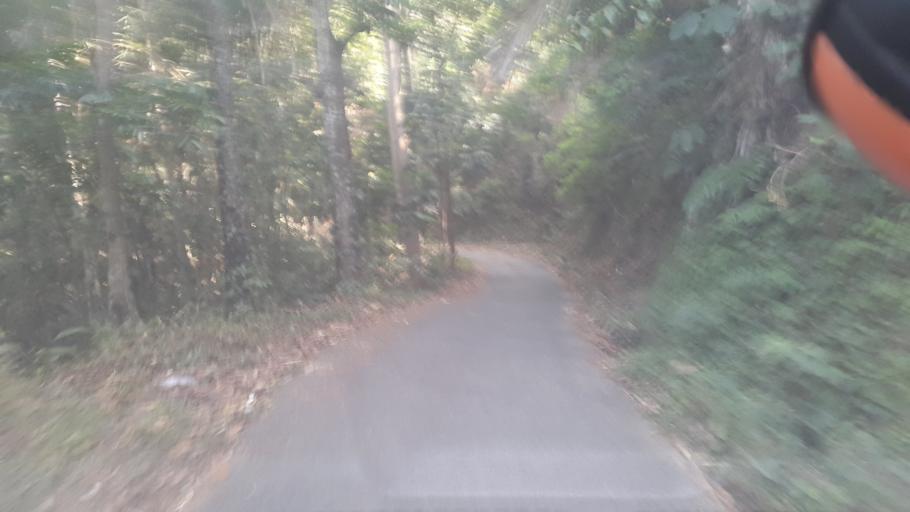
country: ID
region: West Java
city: Tugu
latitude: -6.9379
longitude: 106.4413
